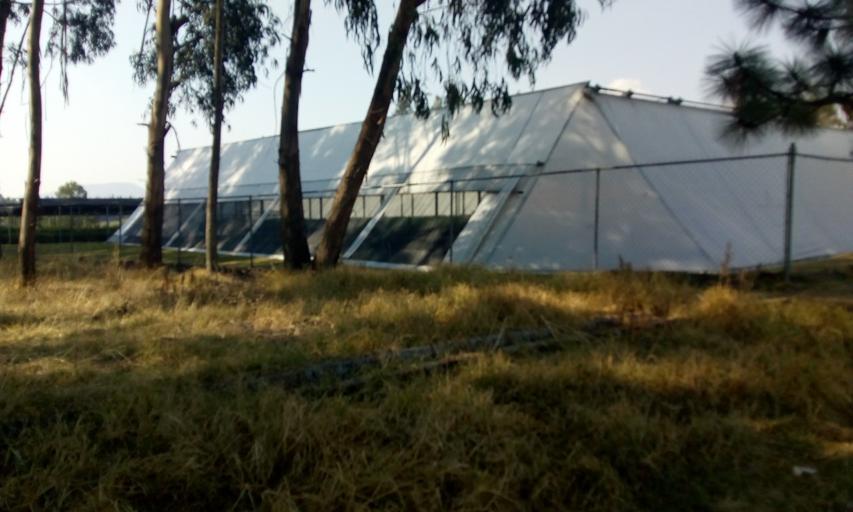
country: MX
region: Mexico
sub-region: Toluca
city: San Antonio Buenavista
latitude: 19.2774
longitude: -99.6989
